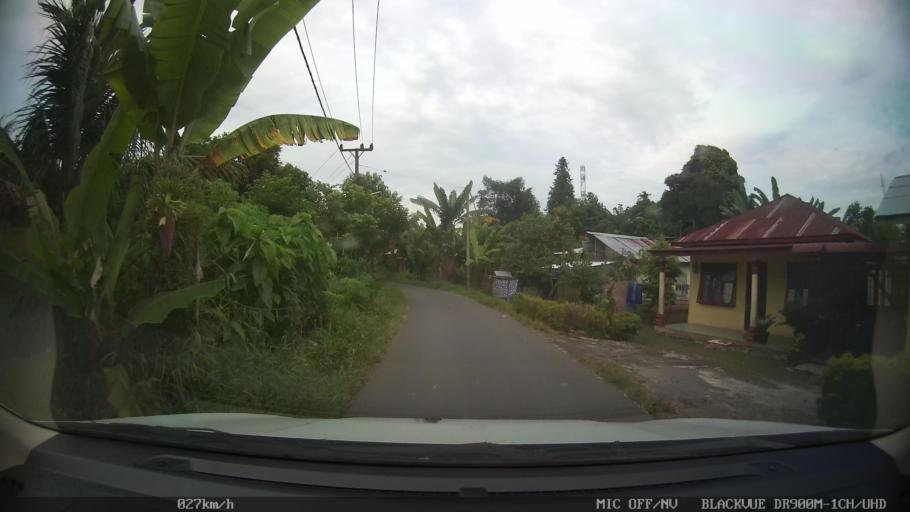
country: ID
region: North Sumatra
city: Sunggal
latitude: 3.6620
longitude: 98.5895
